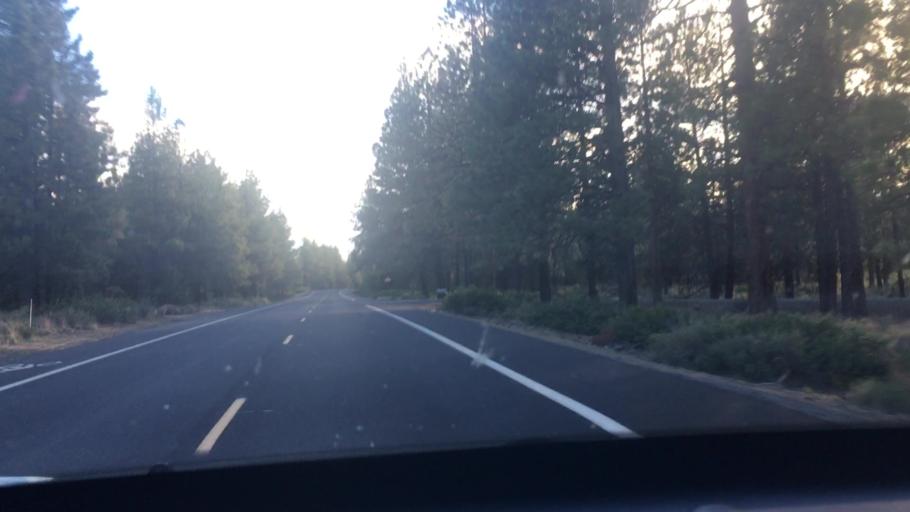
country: US
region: Oregon
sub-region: Deschutes County
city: Deschutes River Woods
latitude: 44.0454
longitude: -121.4017
